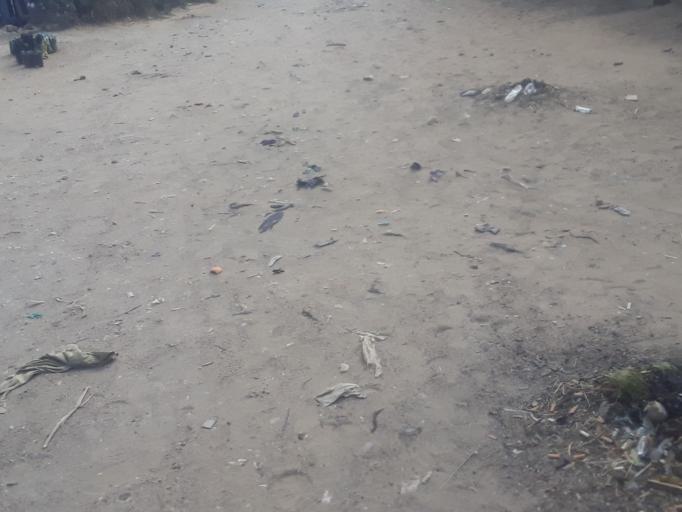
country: ZM
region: Lusaka
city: Lusaka
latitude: -15.3602
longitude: 28.3062
